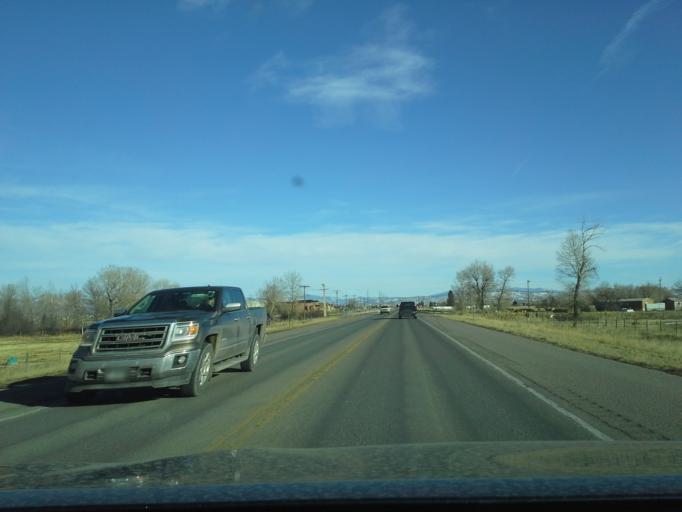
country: US
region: Montana
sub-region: Lewis and Clark County
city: Helena Valley Southeast
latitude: 46.6169
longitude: -111.9640
